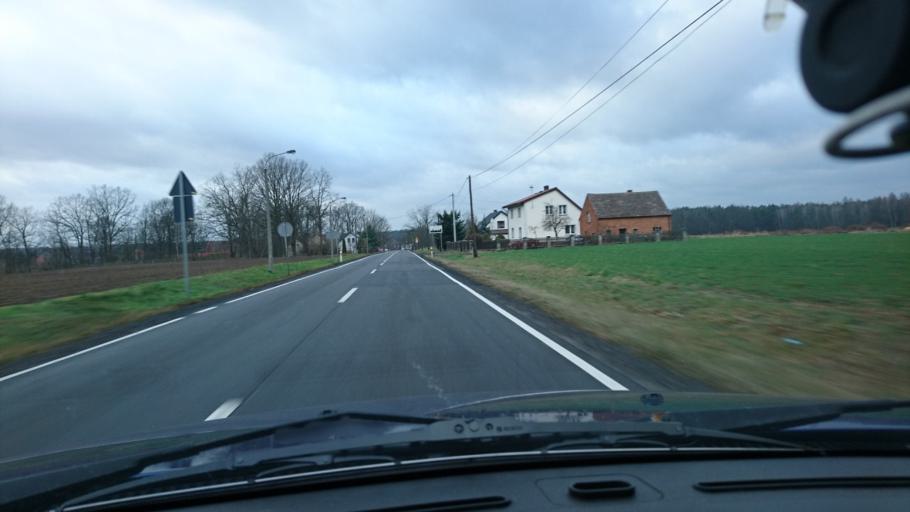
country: PL
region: Opole Voivodeship
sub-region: Powiat oleski
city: Olesno
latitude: 50.9104
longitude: 18.3568
